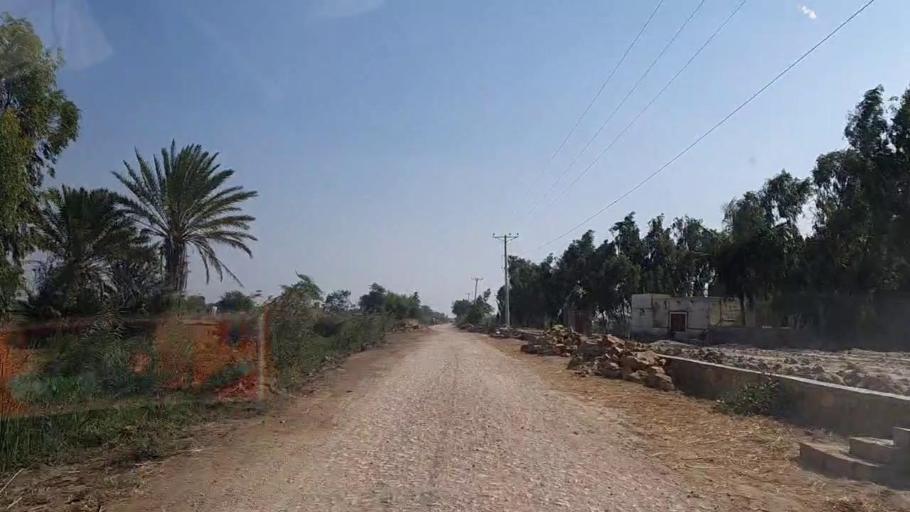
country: PK
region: Sindh
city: Thatta
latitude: 24.7983
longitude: 67.9711
